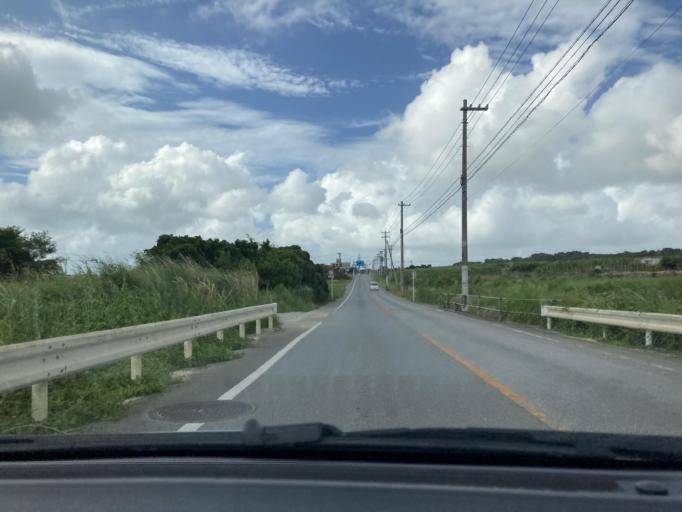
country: JP
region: Okinawa
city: Itoman
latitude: 26.1000
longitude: 127.6980
